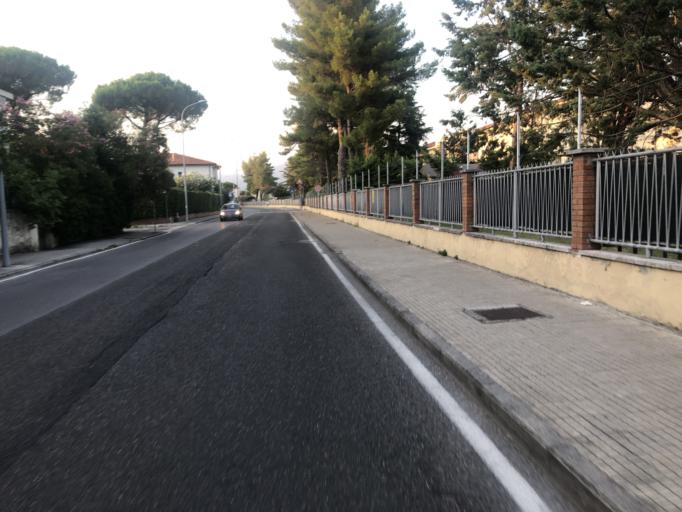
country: IT
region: Tuscany
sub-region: Province of Pisa
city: Pisa
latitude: 43.7292
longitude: 10.4065
